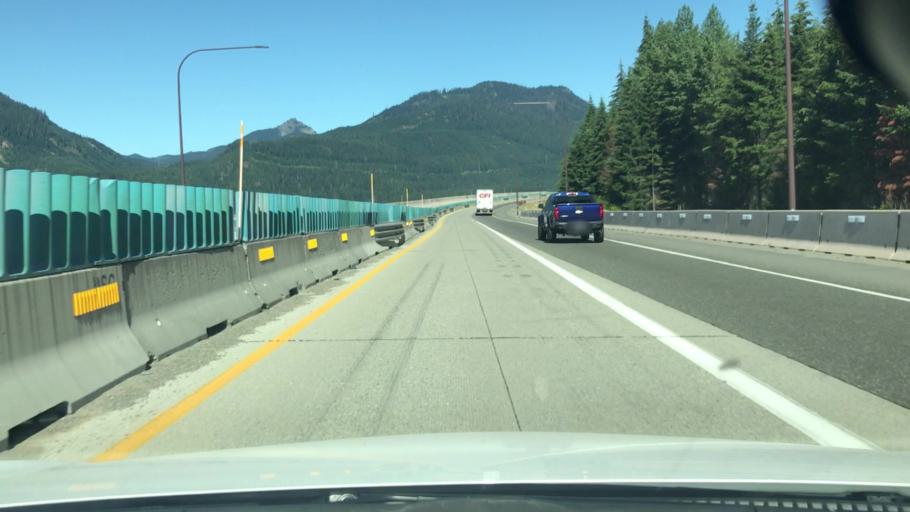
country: US
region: Washington
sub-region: Kittitas County
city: Cle Elum
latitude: 47.3292
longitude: -121.3391
